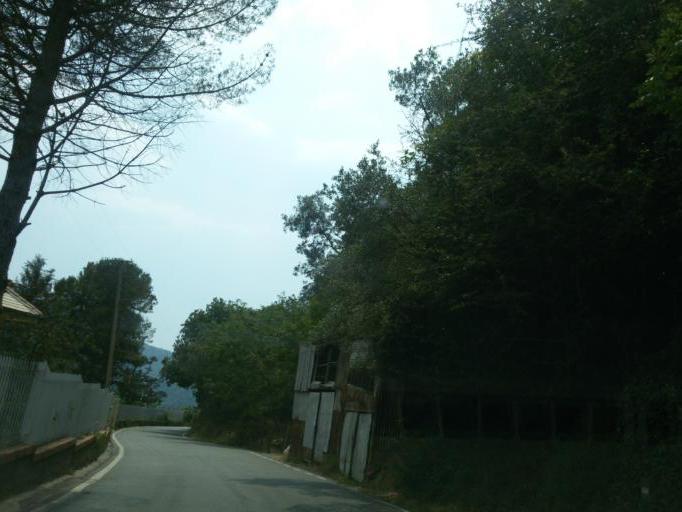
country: IT
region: Liguria
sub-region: Provincia di Genova
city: Bogliasco
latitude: 44.4293
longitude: 9.0158
